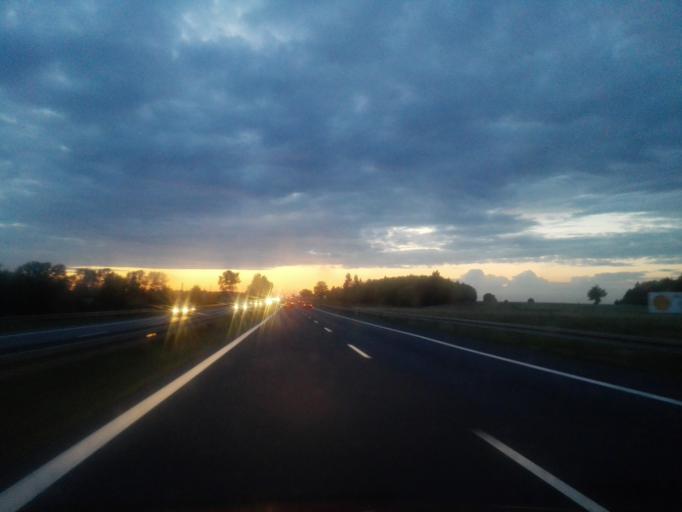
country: PL
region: Lodz Voivodeship
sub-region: Powiat lodzki wschodni
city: Tuszyn
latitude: 51.5587
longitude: 19.5907
